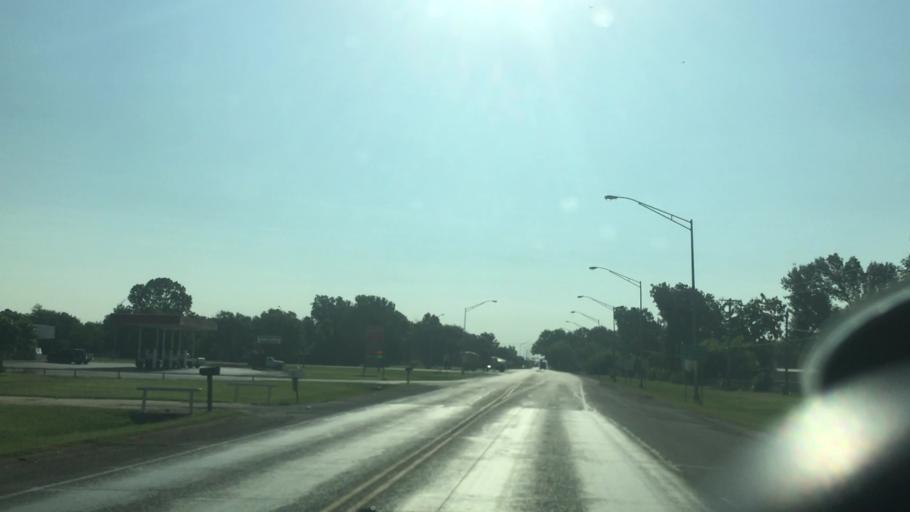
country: US
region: Oklahoma
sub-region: Garvin County
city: Lindsay
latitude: 34.8371
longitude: -97.6179
